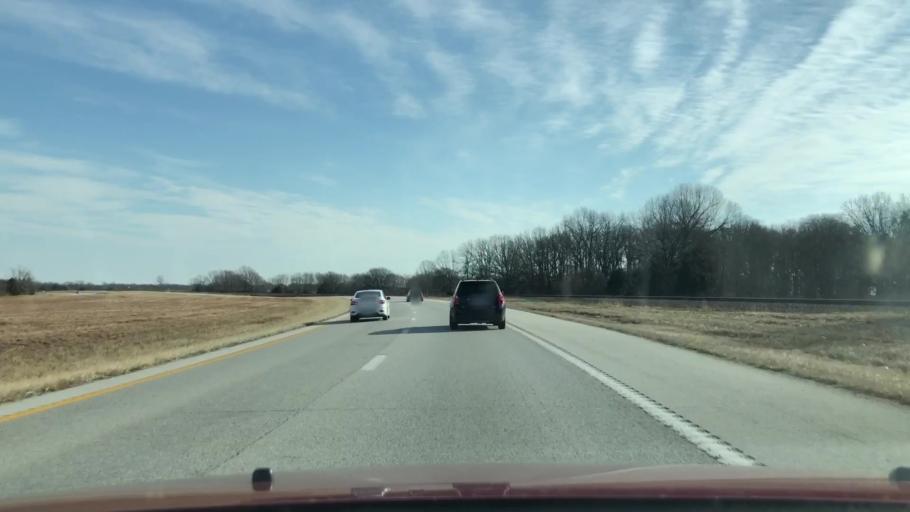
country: US
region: Missouri
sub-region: Webster County
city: Seymour
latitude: 37.1295
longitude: -92.7362
